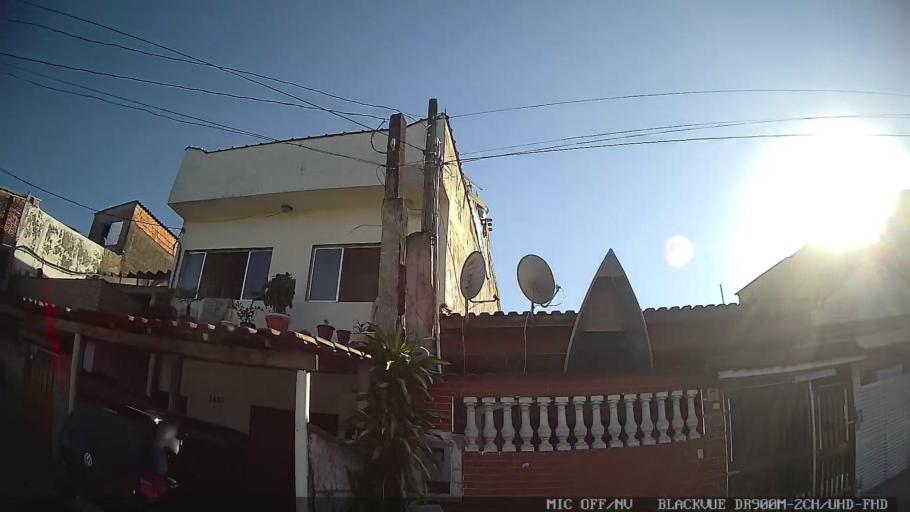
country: BR
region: Sao Paulo
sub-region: Guaruja
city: Guaruja
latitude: -23.9742
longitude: -46.2246
